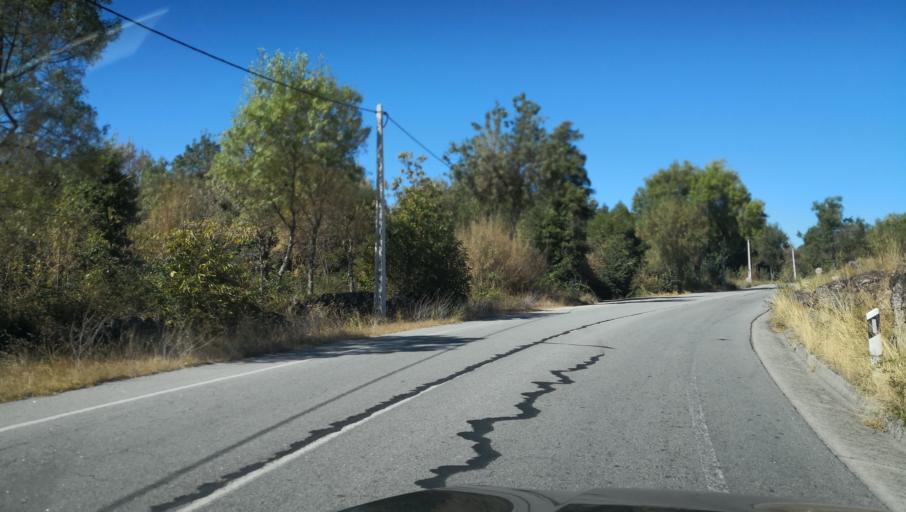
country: PT
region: Vila Real
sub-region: Valpacos
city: Valpacos
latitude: 41.6473
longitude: -7.3207
